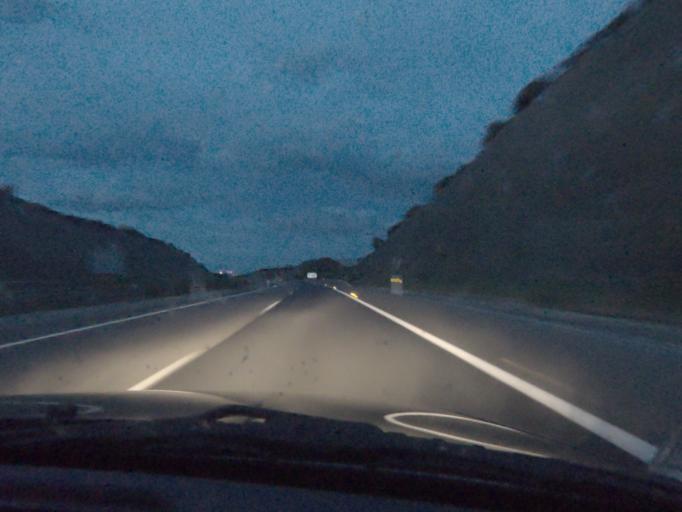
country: ES
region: Extremadura
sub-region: Provincia de Caceres
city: Mirabel
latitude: 39.8864
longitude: -6.2675
